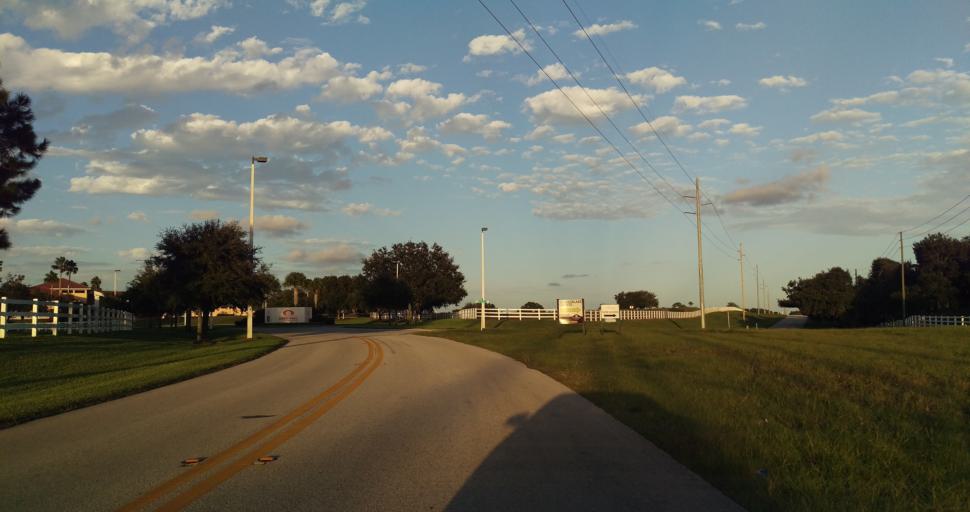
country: US
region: Florida
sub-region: Orange County
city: Lake Butler
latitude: 28.4416
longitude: -81.6308
